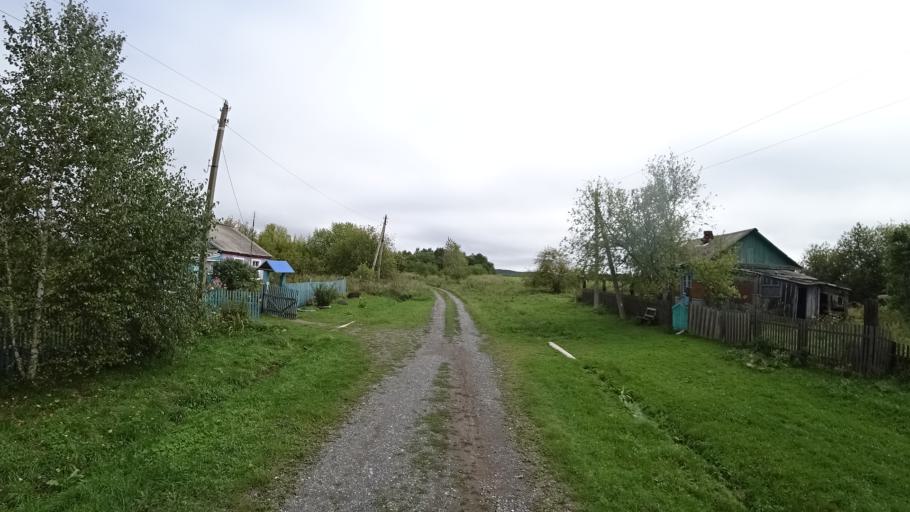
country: RU
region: Primorskiy
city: Lyalichi
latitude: 44.0761
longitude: 132.4800
